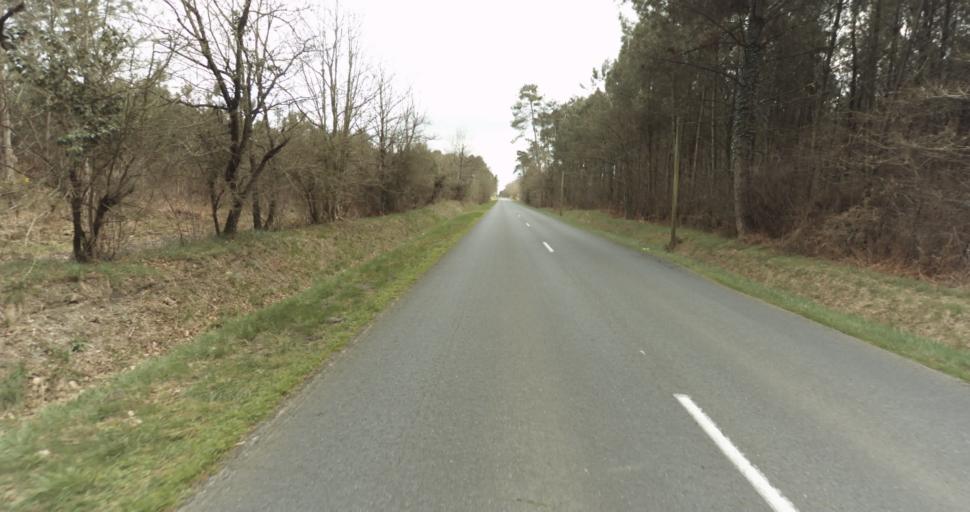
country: FR
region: Aquitaine
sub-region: Departement des Landes
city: Roquefort
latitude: 44.0543
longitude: -0.3829
